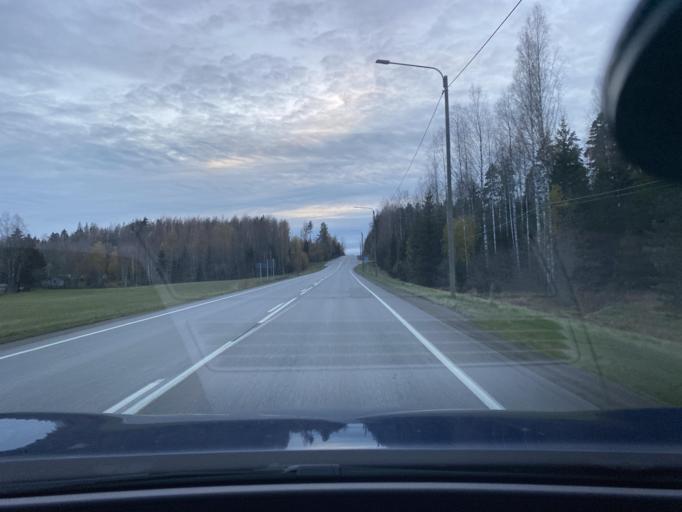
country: FI
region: Uusimaa
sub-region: Helsinki
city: Saukkola
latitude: 60.3882
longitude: 24.0197
